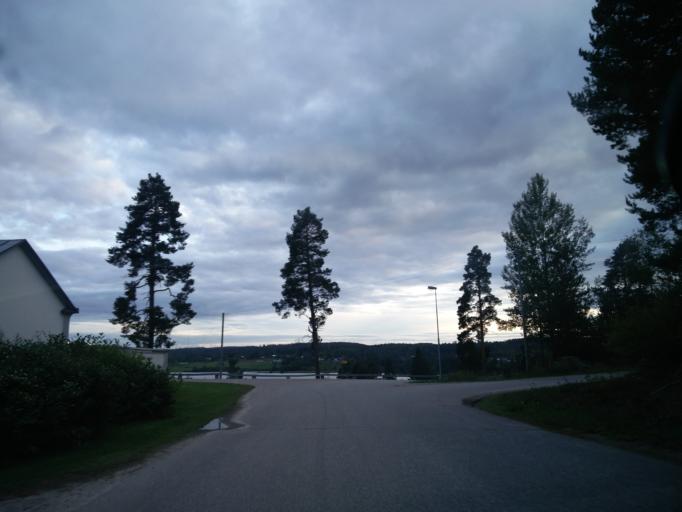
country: SE
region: Vaesternorrland
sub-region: Sundsvalls Kommun
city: Matfors
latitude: 62.3281
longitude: 17.0627
